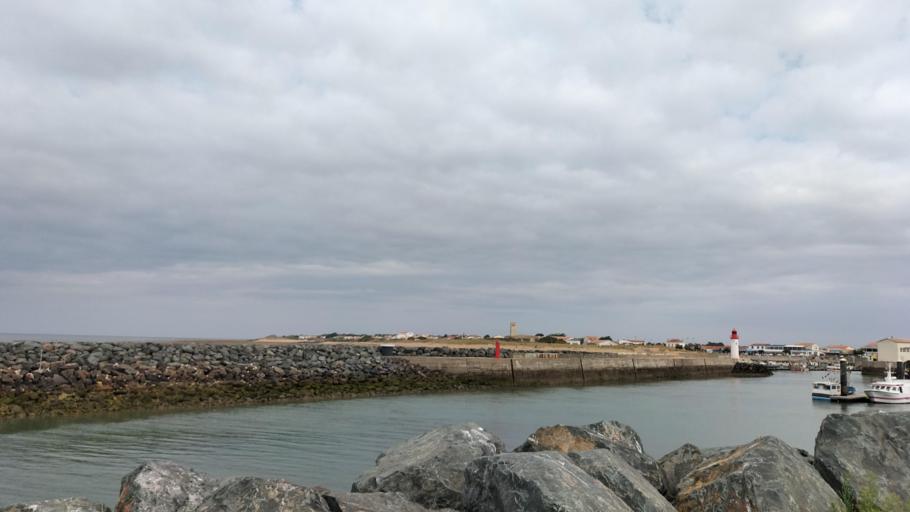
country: FR
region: Poitou-Charentes
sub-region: Departement de la Charente-Maritime
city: Dolus-d'Oleron
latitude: 45.9109
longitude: -1.3276
